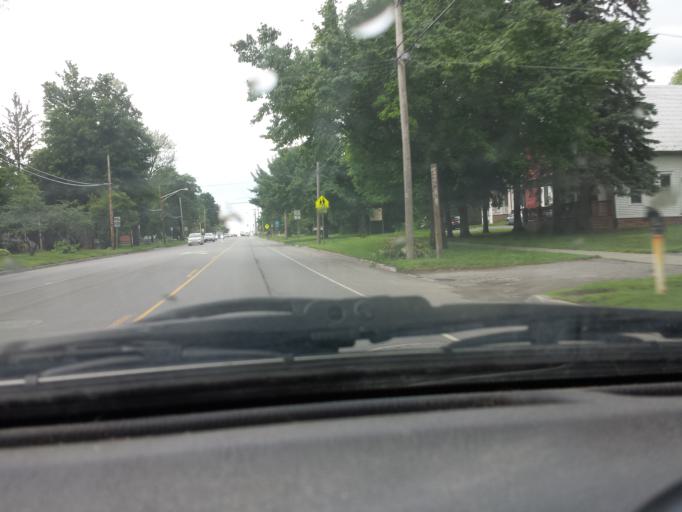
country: US
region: New York
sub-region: St. Lawrence County
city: Potsdam
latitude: 44.6748
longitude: -74.9868
